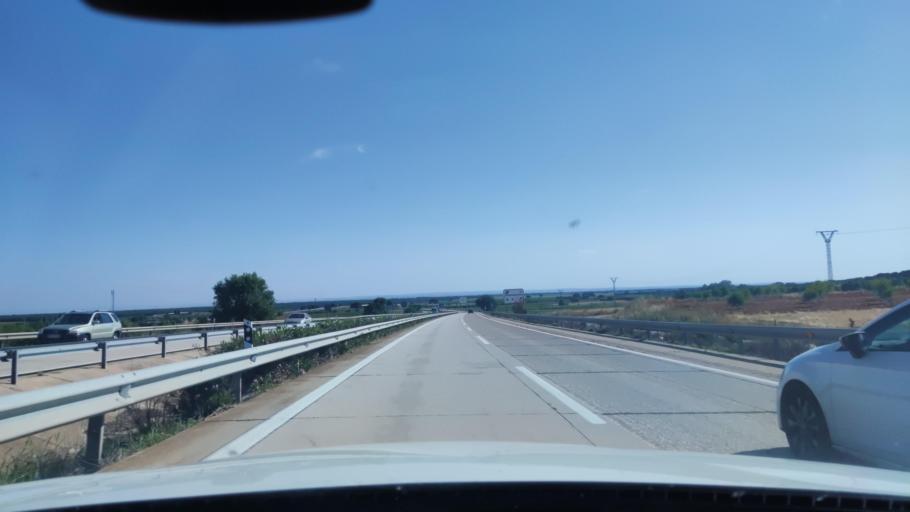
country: ES
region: Castille-La Mancha
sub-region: Provincia de Cuenca
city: Pozoamargo
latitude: 39.3687
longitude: -2.2008
